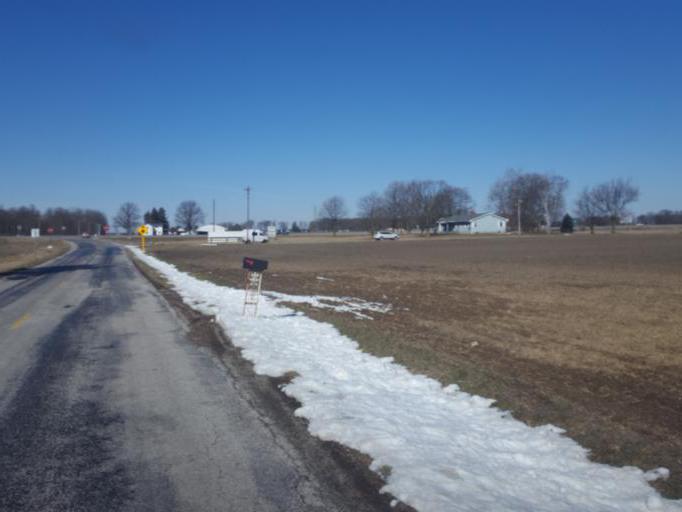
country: US
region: Ohio
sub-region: Marion County
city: Marion
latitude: 40.6520
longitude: -83.1026
